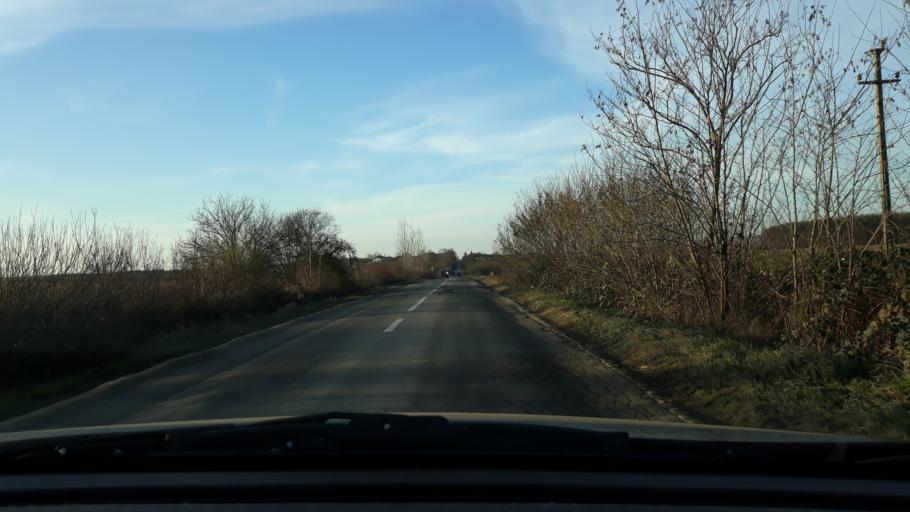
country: RO
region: Bihor
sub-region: Comuna Suplacu de Barcau
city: Suplacu de Barcau
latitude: 47.2692
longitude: 22.4976
